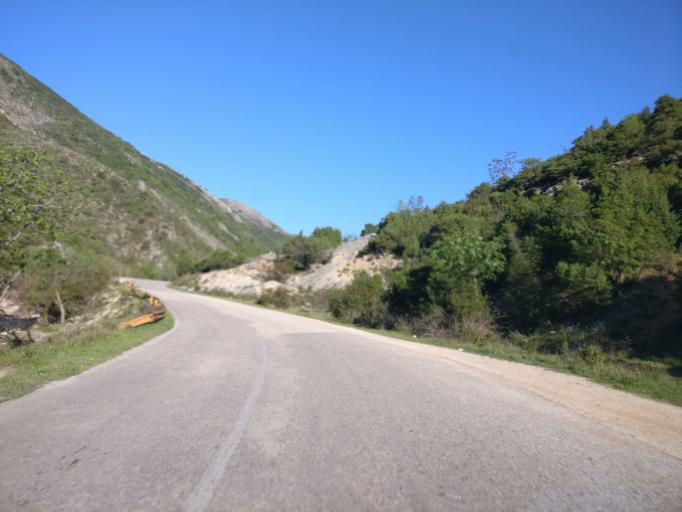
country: BA
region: Federation of Bosnia and Herzegovina
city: Stolac
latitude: 43.0828
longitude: 18.0100
